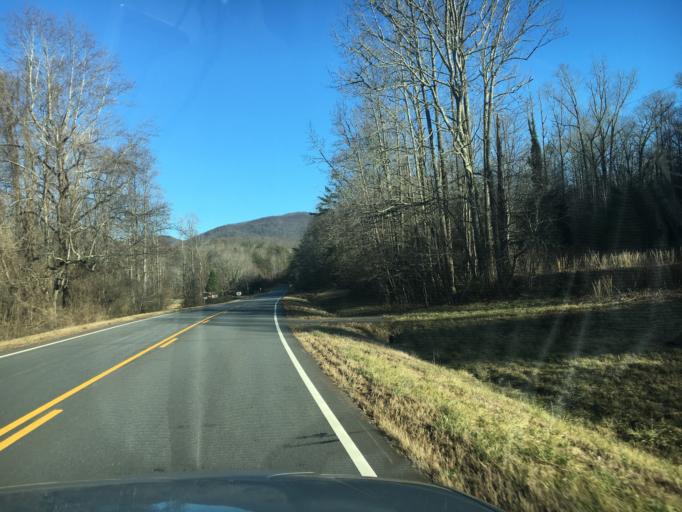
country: US
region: Georgia
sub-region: White County
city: Cleveland
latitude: 34.6688
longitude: -83.8653
